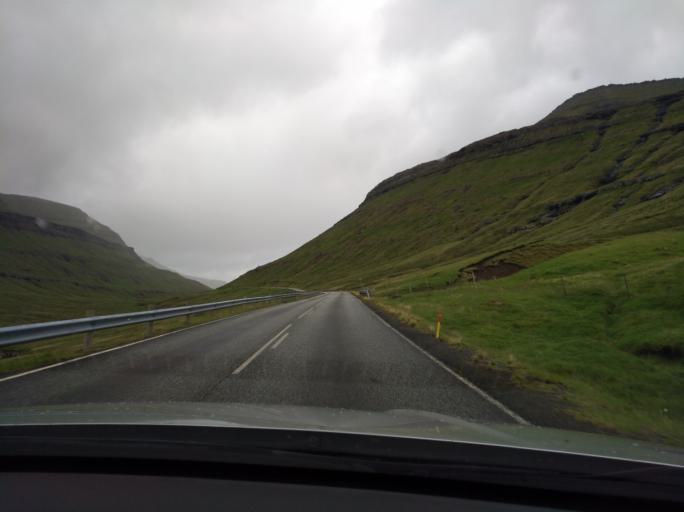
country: FO
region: Eysturoy
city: Fuglafjordur
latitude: 62.2249
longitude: -6.8800
